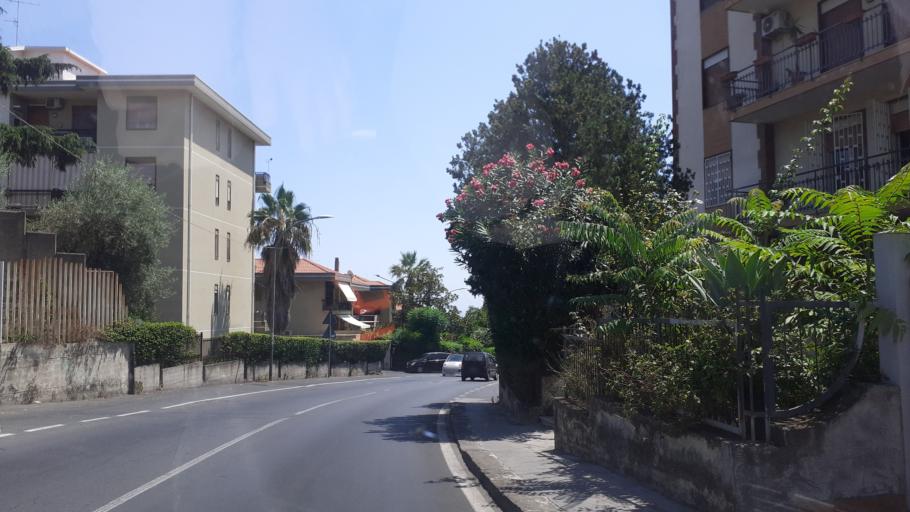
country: IT
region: Sicily
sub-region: Catania
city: Canalicchio
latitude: 37.5387
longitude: 15.0960
